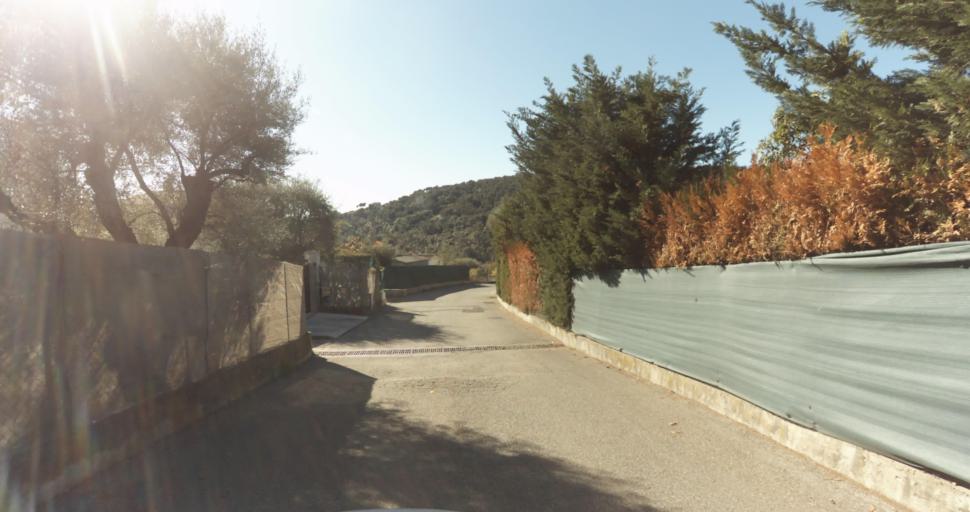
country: FR
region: Provence-Alpes-Cote d'Azur
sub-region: Departement des Alpes-Maritimes
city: Saint-Paul-de-Vence
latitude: 43.7097
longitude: 7.1288
